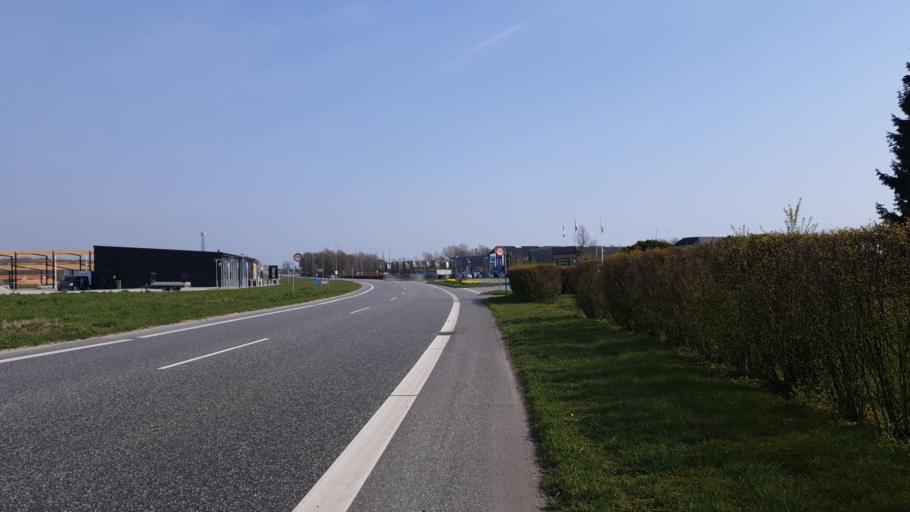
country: DK
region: Central Jutland
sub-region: Hedensted Kommune
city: Hedensted
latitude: 55.7821
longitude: 9.6882
